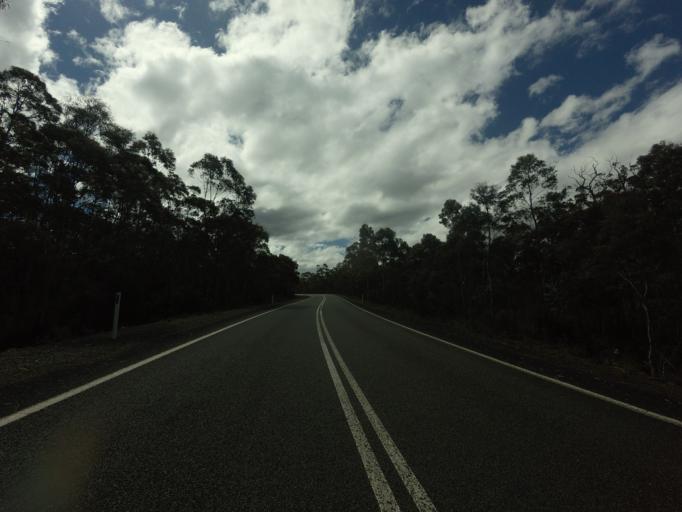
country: AU
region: Tasmania
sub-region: Break O'Day
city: St Helens
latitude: -42.0121
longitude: 147.9066
